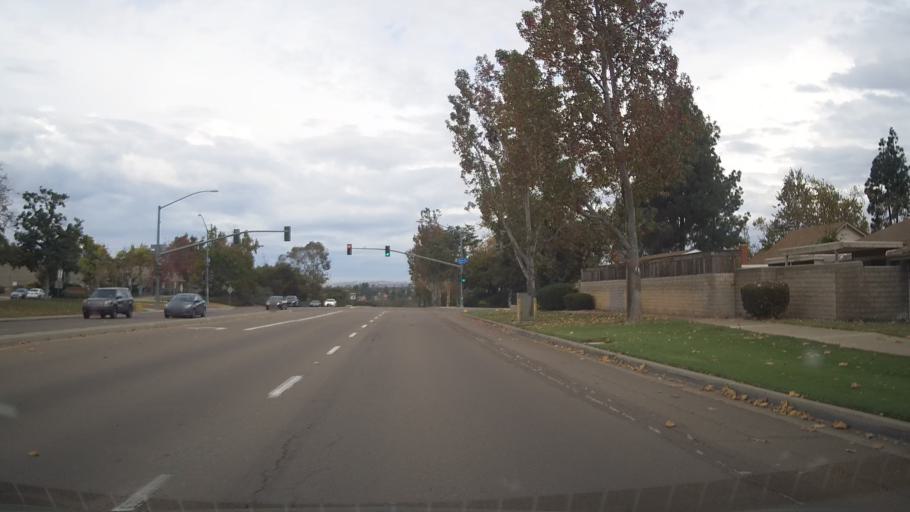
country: US
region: California
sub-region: San Diego County
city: La Mesa
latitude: 32.8251
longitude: -117.1039
